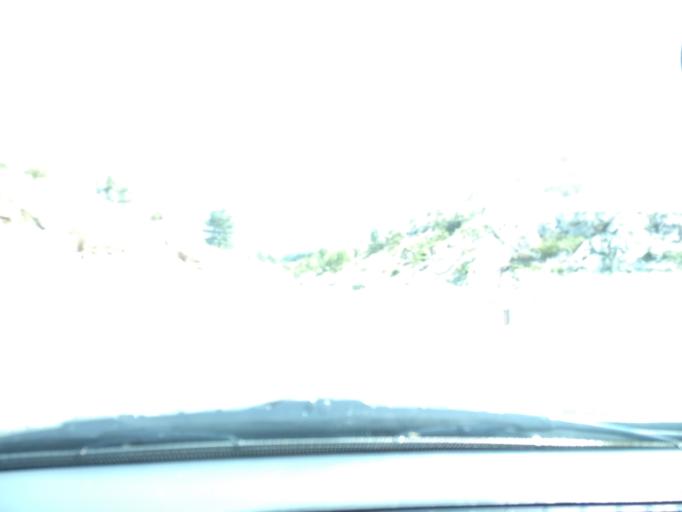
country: ME
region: Kotor
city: Kotor
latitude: 42.4326
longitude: 18.8095
